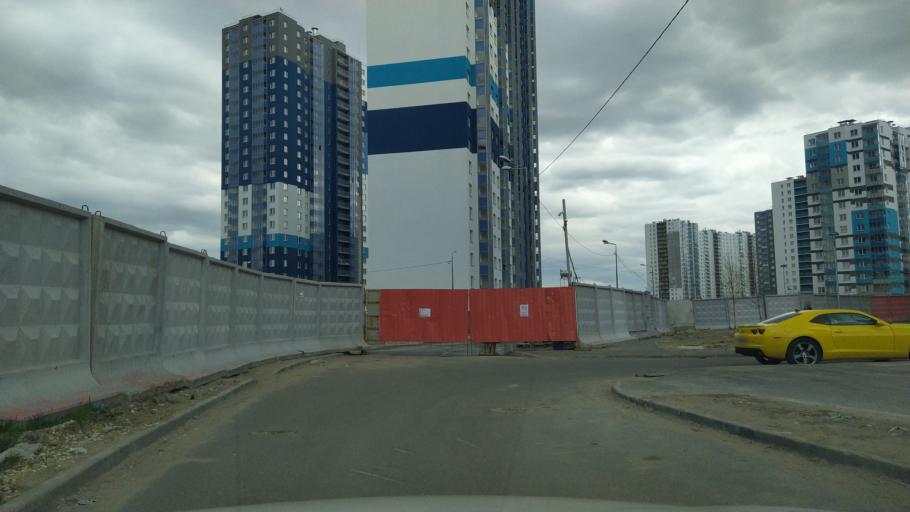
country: RU
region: Leningrad
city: Murino
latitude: 60.0373
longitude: 30.4556
